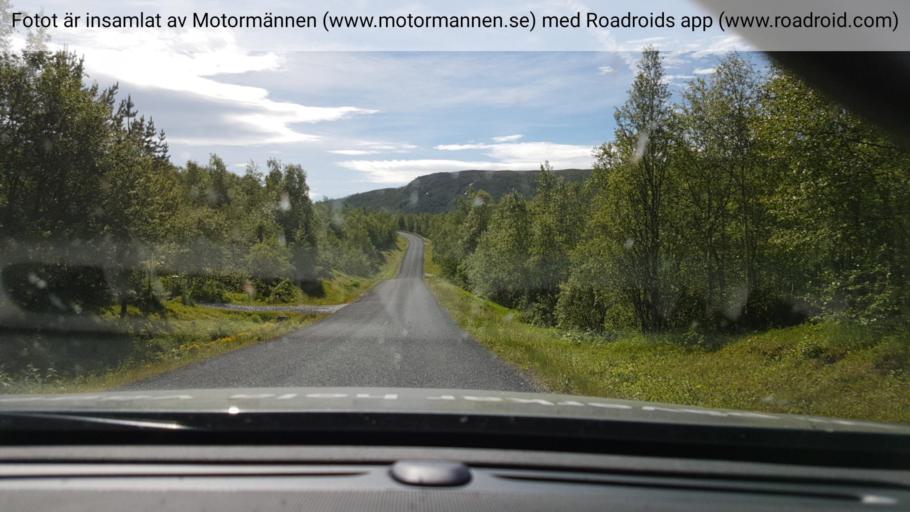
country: SE
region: Vaesterbotten
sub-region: Vilhelmina Kommun
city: Sjoberg
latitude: 65.2893
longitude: 15.2936
